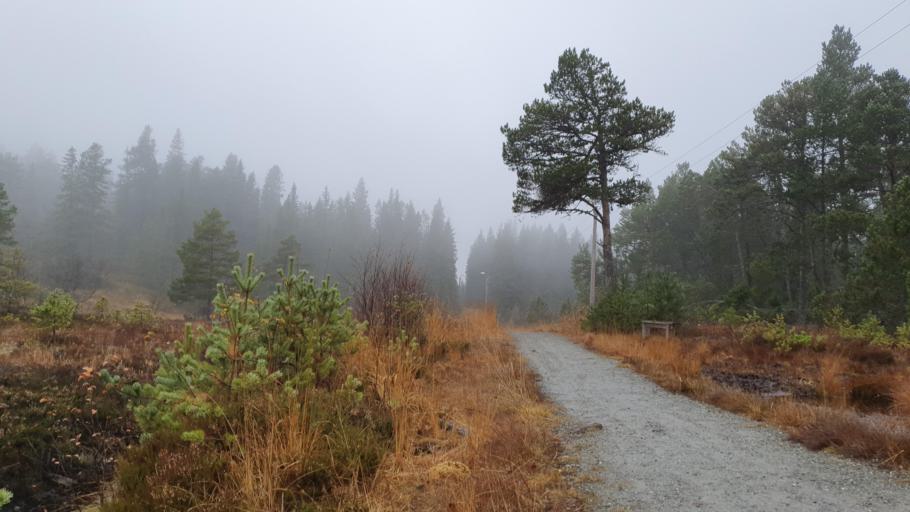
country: NO
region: Sor-Trondelag
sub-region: Trondheim
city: Trondheim
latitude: 63.4135
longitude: 10.3165
